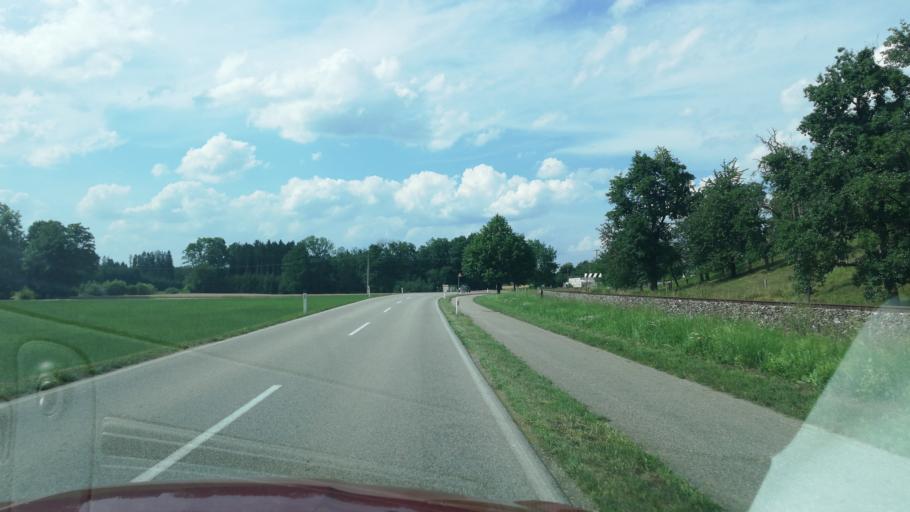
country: AT
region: Upper Austria
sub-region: Politischer Bezirk Vocklabruck
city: Puhret
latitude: 48.0287
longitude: 13.7045
